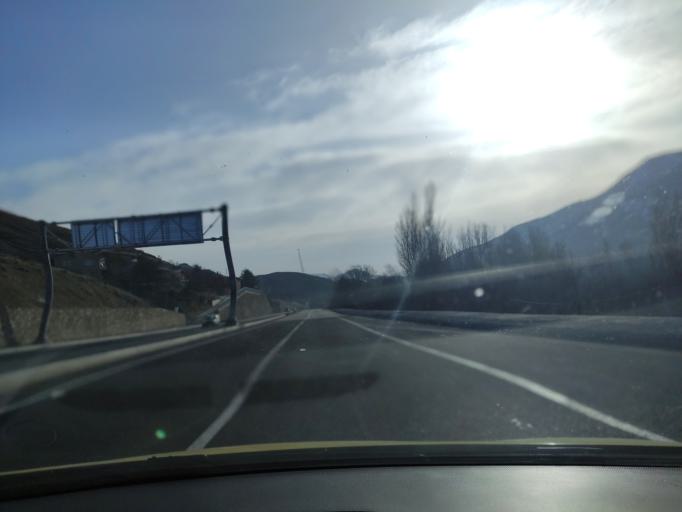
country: TR
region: Gumushane
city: Kale
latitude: 40.4050
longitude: 39.6136
